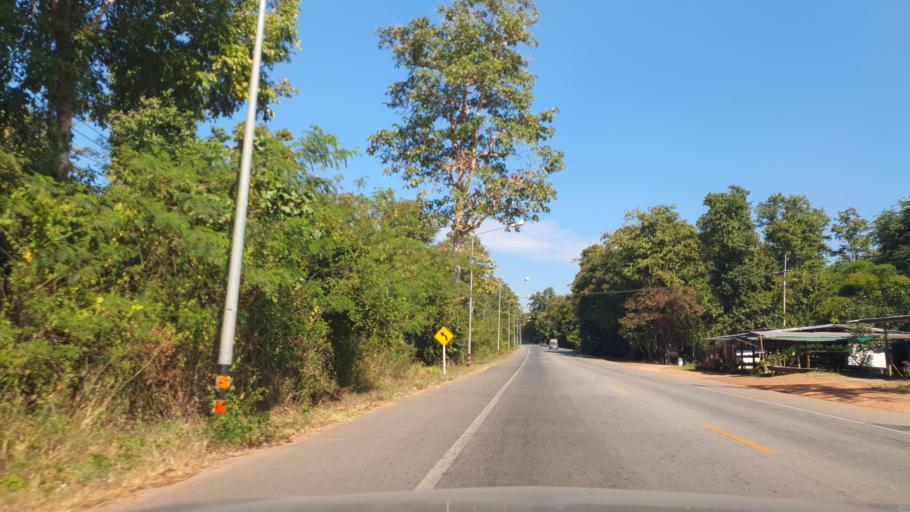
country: TH
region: Sakon Nakhon
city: Phu Phan
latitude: 17.0988
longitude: 103.9911
